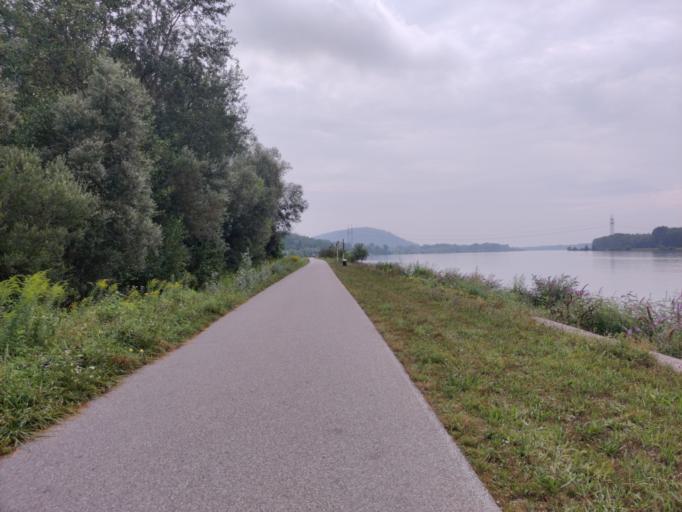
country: AT
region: Upper Austria
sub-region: Politischer Bezirk Urfahr-Umgebung
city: Steyregg
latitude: 48.2724
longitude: 14.3704
